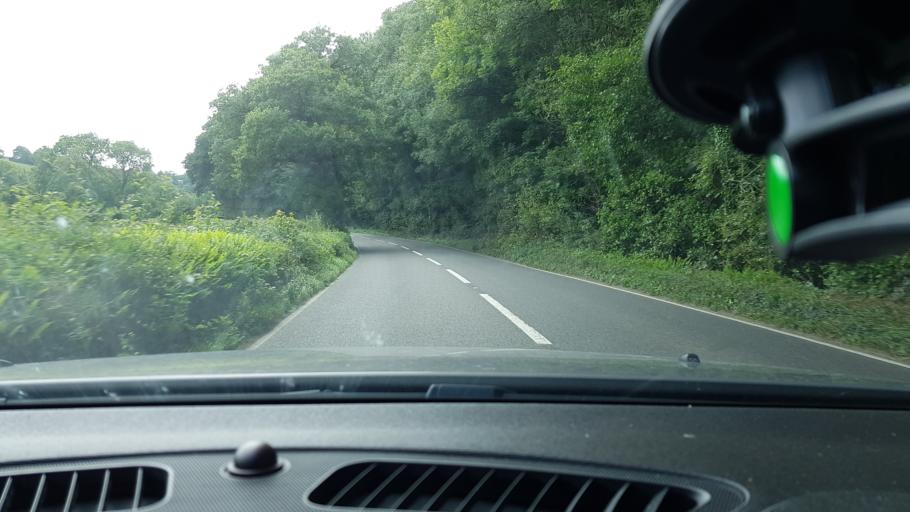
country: GB
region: England
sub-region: Cornwall
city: Camelford
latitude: 50.5768
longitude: -4.7388
